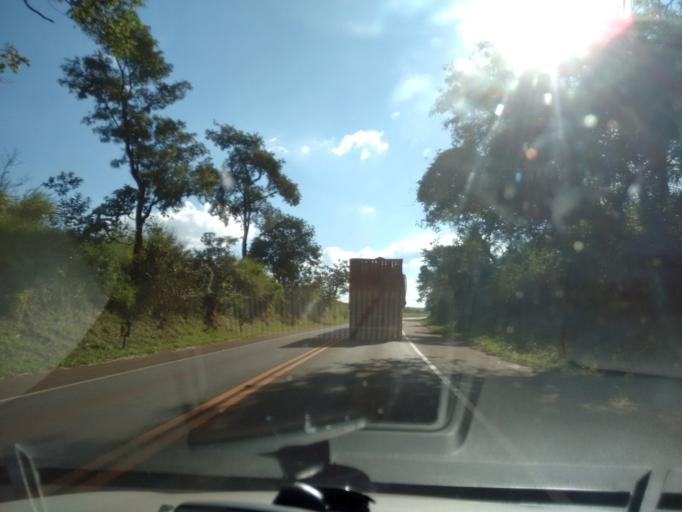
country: BR
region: Sao Paulo
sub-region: Americo Brasiliense
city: Americo Brasiliense
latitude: -21.6216
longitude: -48.0191
